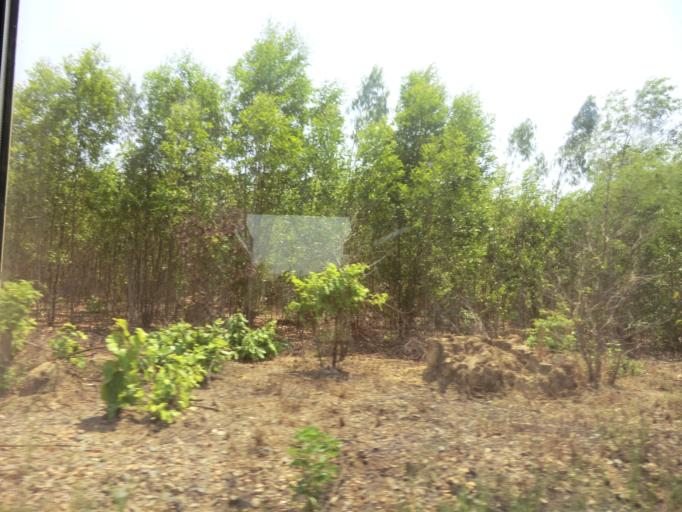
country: VN
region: Binh Thuan
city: Thuan Nam
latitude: 10.9214
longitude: 107.8793
